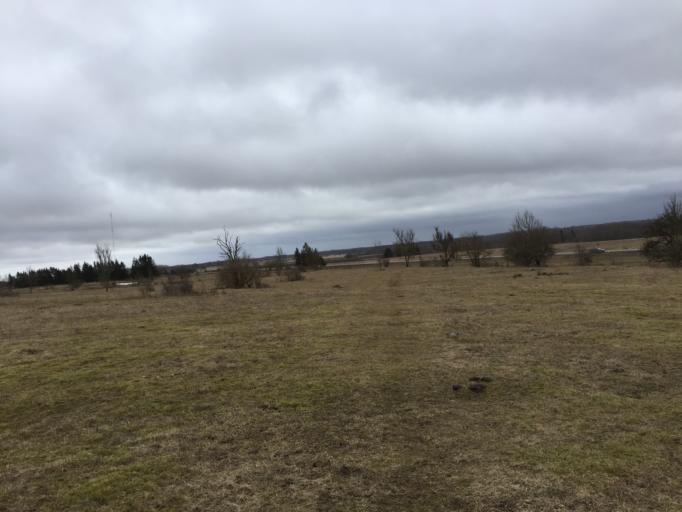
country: EE
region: Laeaene
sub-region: Lihula vald
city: Lihula
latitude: 58.7278
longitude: 23.9280
